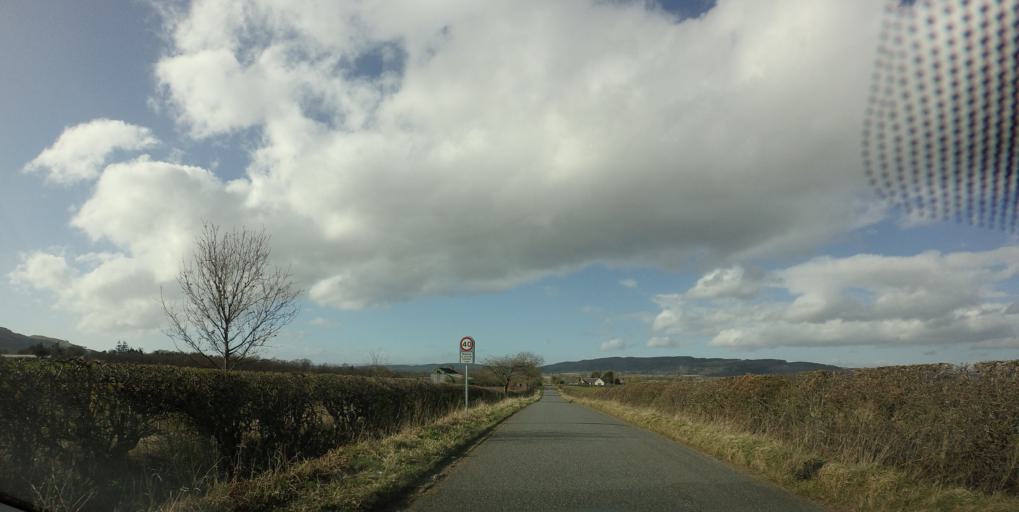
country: GB
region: Scotland
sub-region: Perth and Kinross
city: Bridge of Earn
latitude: 56.3240
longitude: -3.3753
